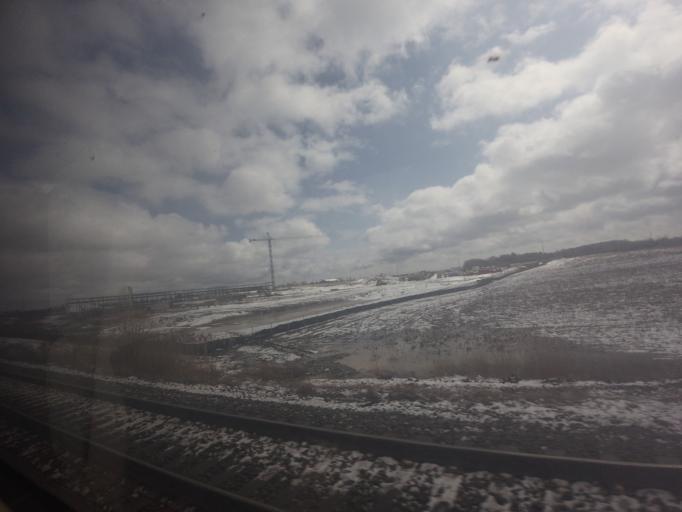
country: CA
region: Ontario
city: Ajax
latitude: 43.8435
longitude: -79.0581
